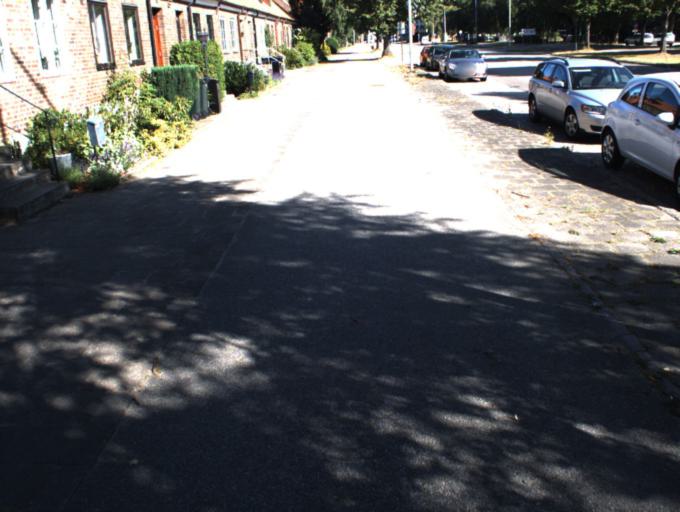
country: SE
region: Skane
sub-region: Helsingborg
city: Helsingborg
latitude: 56.0133
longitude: 12.7257
